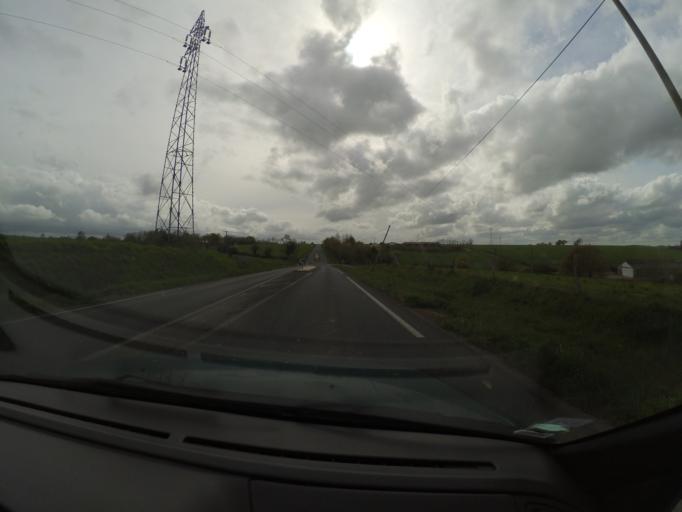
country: FR
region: Pays de la Loire
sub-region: Departement de Maine-et-Loire
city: Saint-Laurent-des-Autels
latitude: 47.2932
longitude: -1.1773
